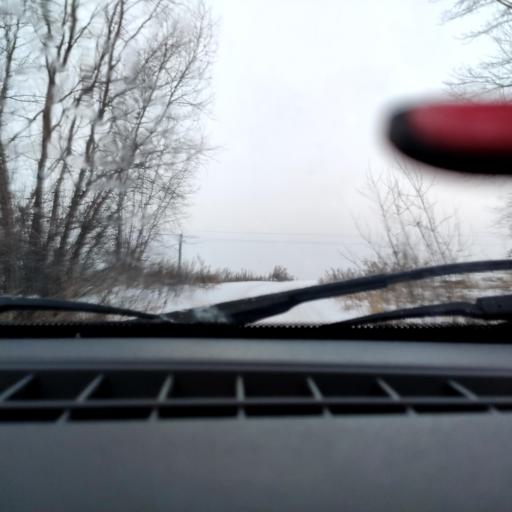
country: RU
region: Bashkortostan
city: Blagoveshchensk
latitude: 54.9127
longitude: 55.9927
